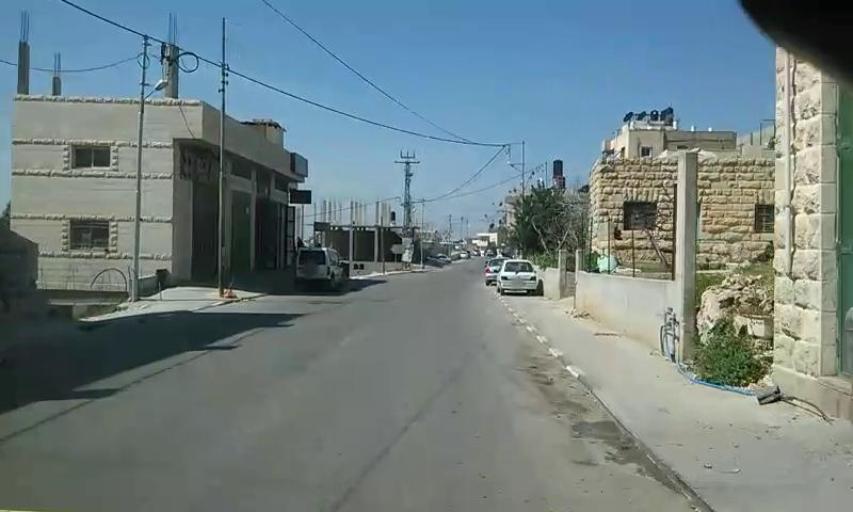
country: PS
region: West Bank
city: Husan
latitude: 31.7067
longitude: 35.1358
